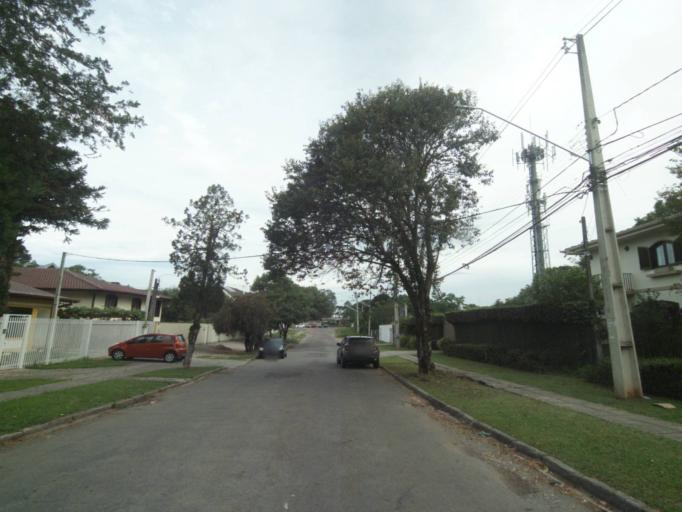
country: BR
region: Parana
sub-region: Pinhais
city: Pinhais
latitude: -25.4231
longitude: -49.2285
